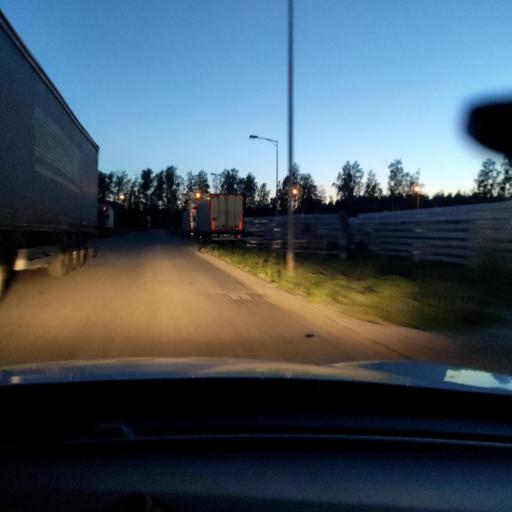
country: RU
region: Tatarstan
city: Osinovo
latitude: 55.8491
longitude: 48.8347
